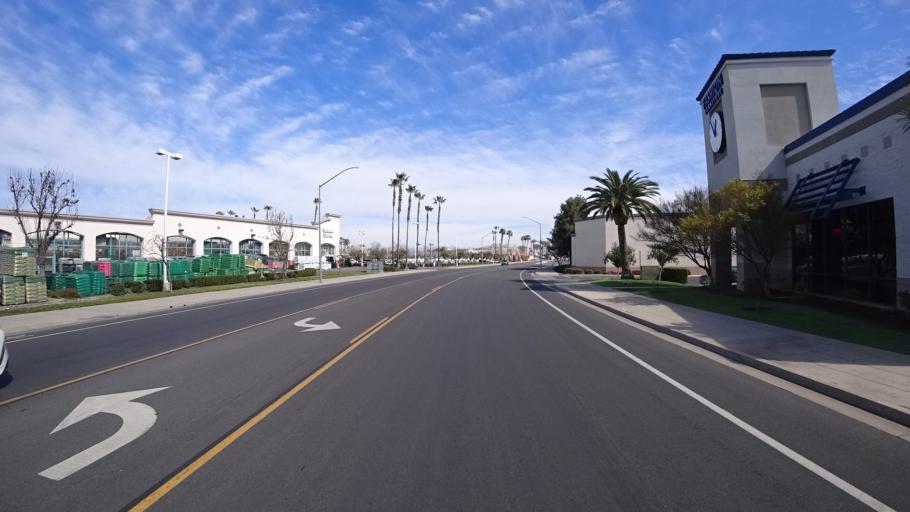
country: US
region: California
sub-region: Fresno County
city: Clovis
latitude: 36.8460
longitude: -119.7942
